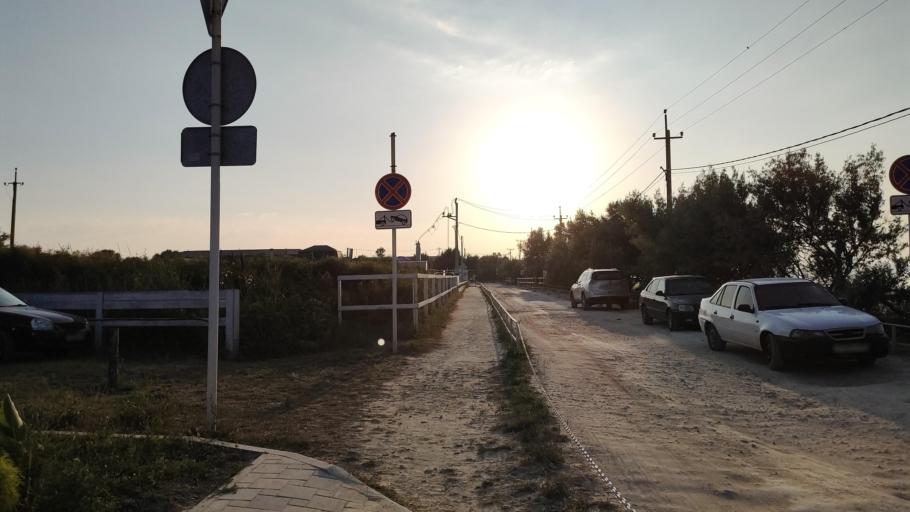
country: RU
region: Krasnodarskiy
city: Blagovetschenskaya
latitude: 45.0658
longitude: 37.0429
